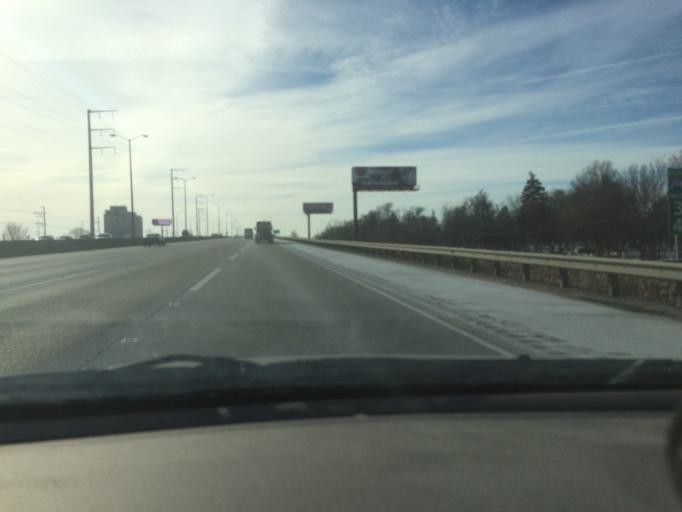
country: US
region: Illinois
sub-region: DuPage County
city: Elmhurst
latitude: 41.9121
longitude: -87.9199
